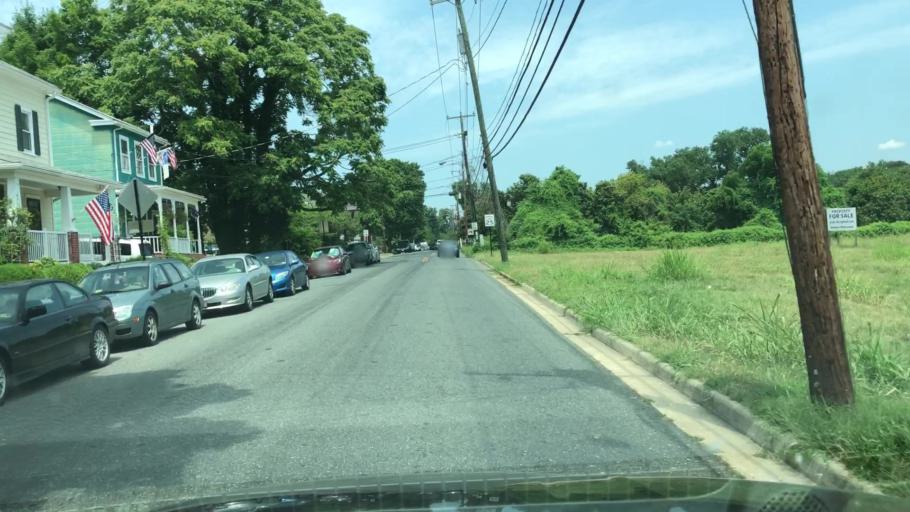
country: US
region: Virginia
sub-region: City of Fredericksburg
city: Fredericksburg
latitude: 38.3055
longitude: -77.4595
